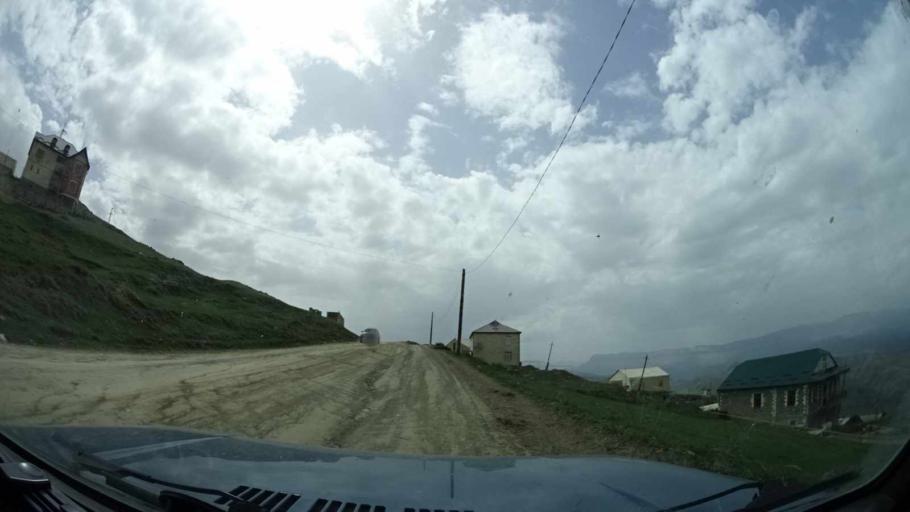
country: RU
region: Dagestan
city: Kubachi
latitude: 42.0913
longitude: 47.5884
